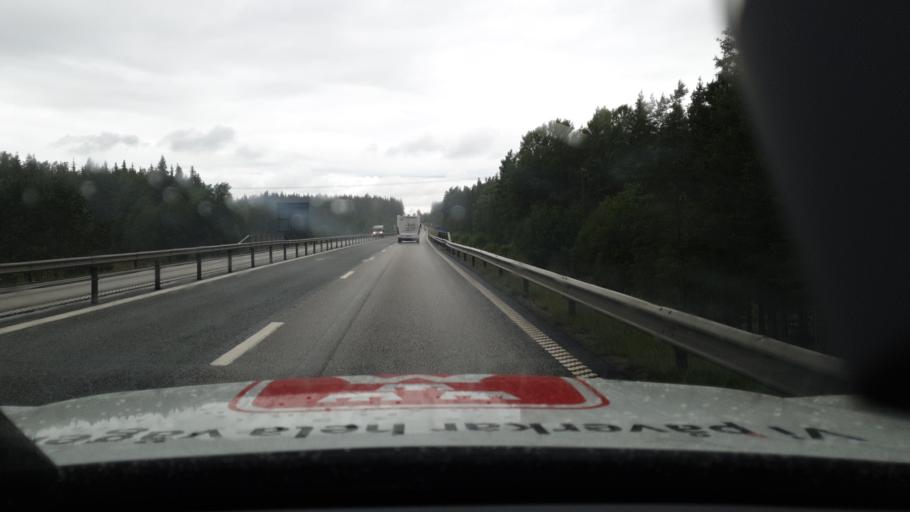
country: SE
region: Joenkoeping
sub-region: Nassjo Kommun
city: Malmback
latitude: 57.6933
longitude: 14.4491
